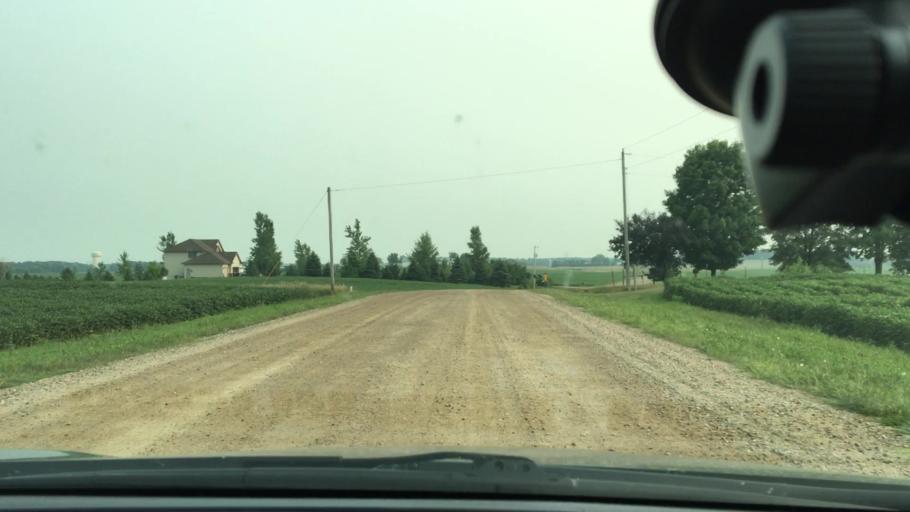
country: US
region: Minnesota
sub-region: Wright County
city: Albertville
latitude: 45.2457
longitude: -93.6273
